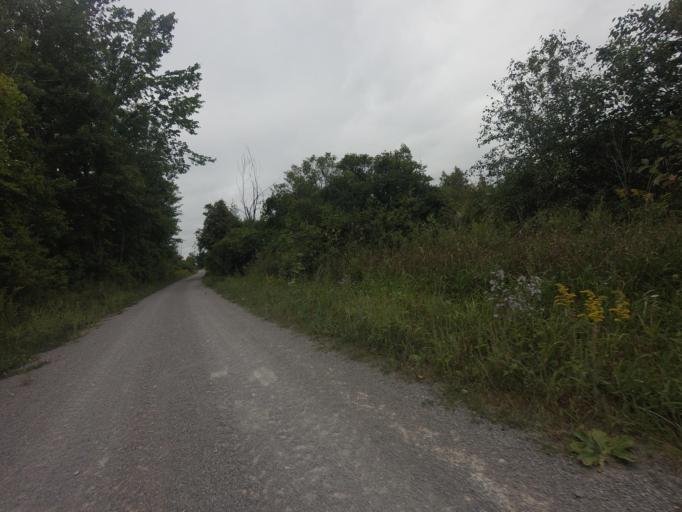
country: CA
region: Ontario
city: Omemee
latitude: 44.4239
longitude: -78.7753
